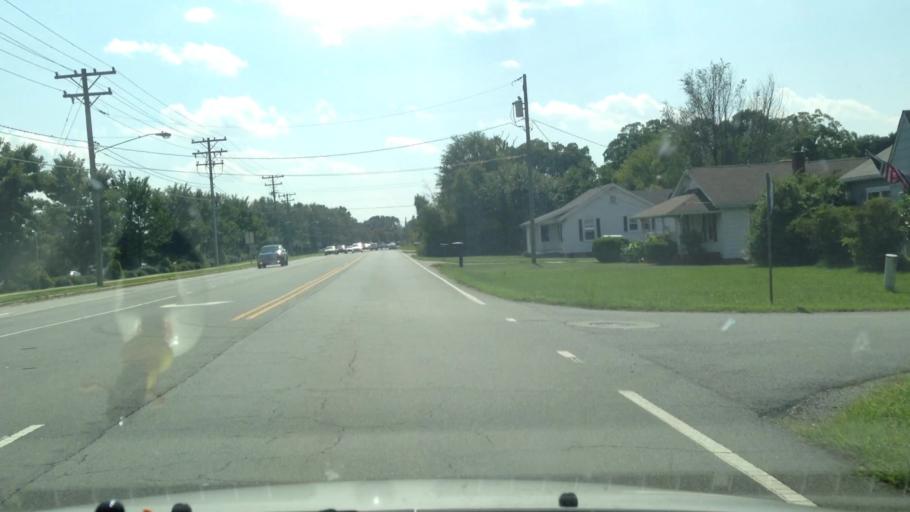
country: US
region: North Carolina
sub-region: Forsyth County
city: Kernersville
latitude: 36.1300
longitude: -80.0586
